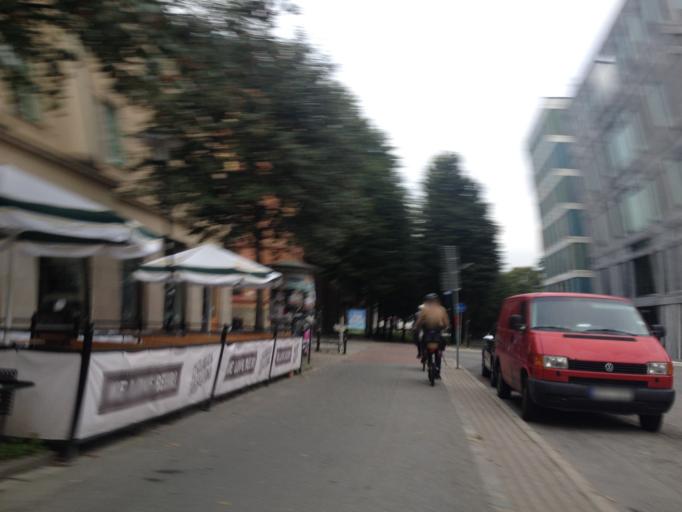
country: SE
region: OErebro
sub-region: Orebro Kommun
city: Orebro
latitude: 59.2780
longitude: 15.2150
